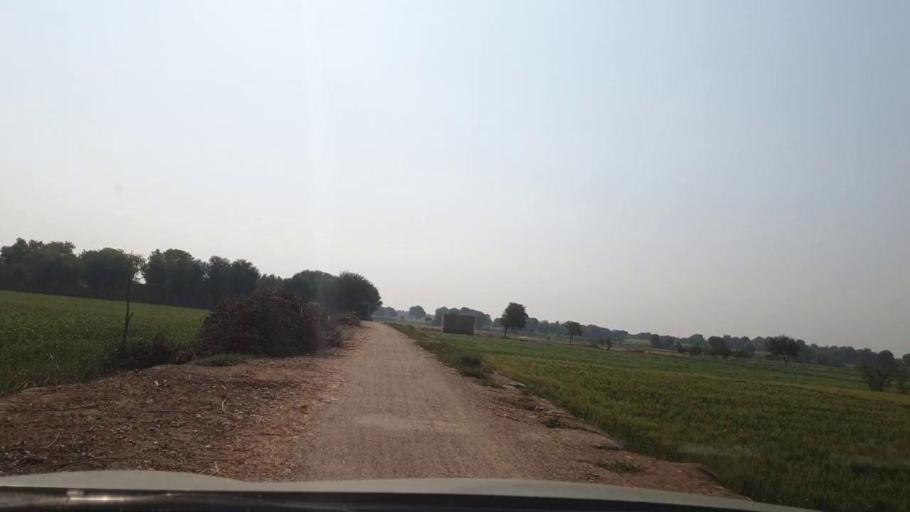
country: PK
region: Sindh
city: Tando Allahyar
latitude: 25.5306
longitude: 68.7901
